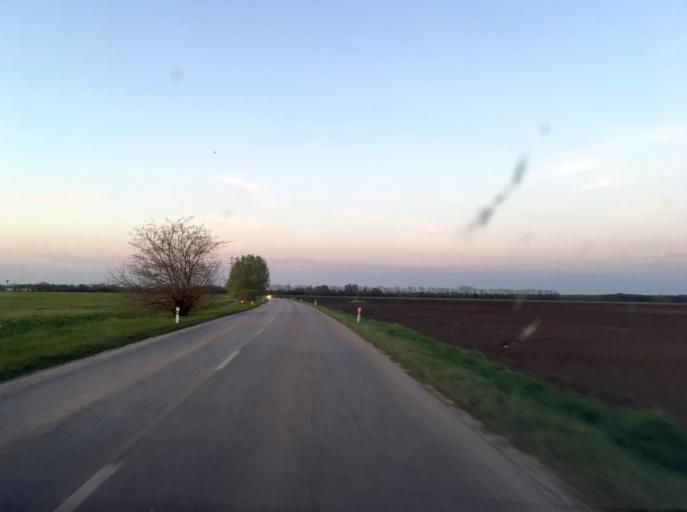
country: SK
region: Nitriansky
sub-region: Okres Nove Zamky
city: Nove Zamky
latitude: 47.9451
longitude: 18.1336
